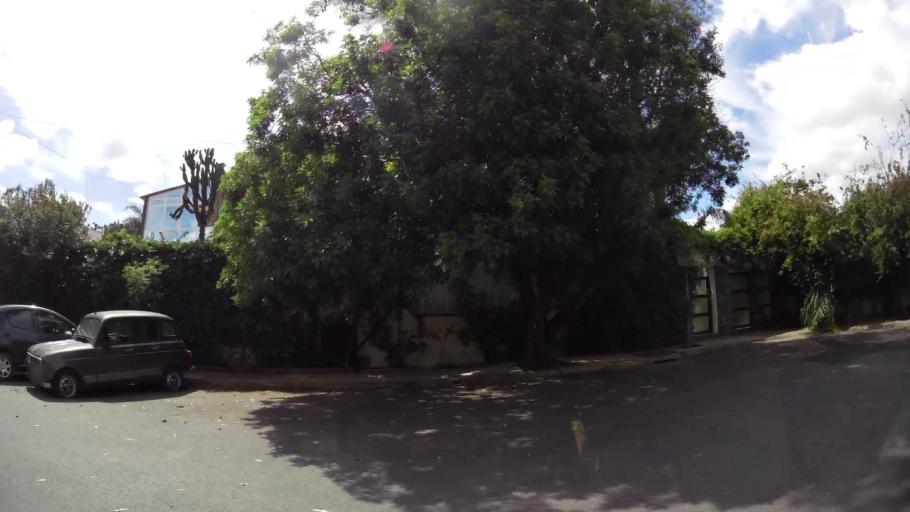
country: MA
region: Grand Casablanca
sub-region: Casablanca
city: Casablanca
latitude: 33.5596
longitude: -7.6275
